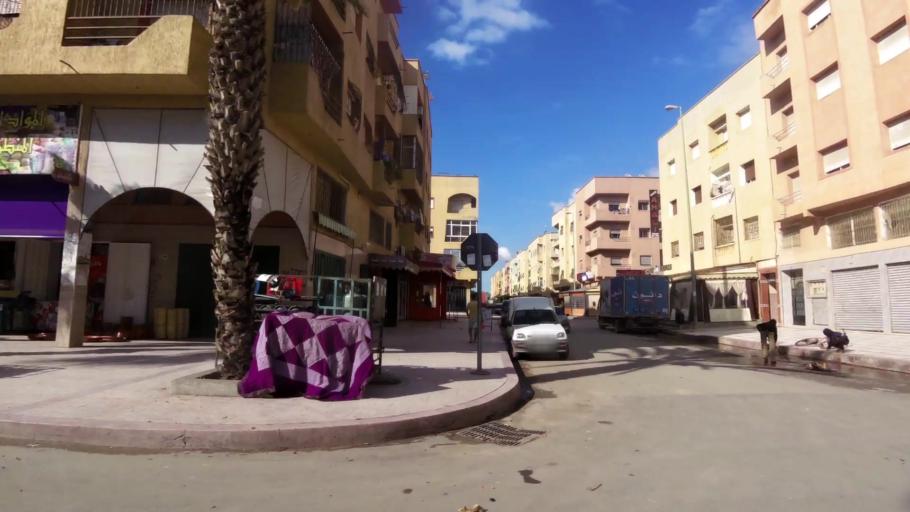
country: MA
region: Chaouia-Ouardigha
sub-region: Settat Province
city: Berrechid
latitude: 33.2749
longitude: -7.5798
